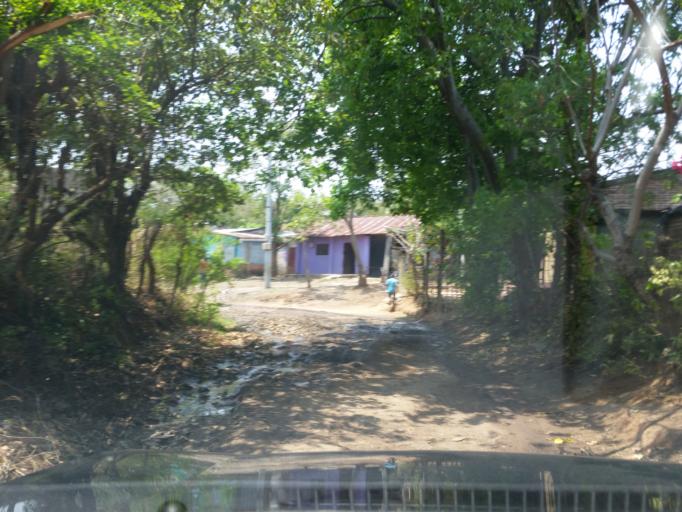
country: NI
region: Granada
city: Granada
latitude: 11.9191
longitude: -85.9612
